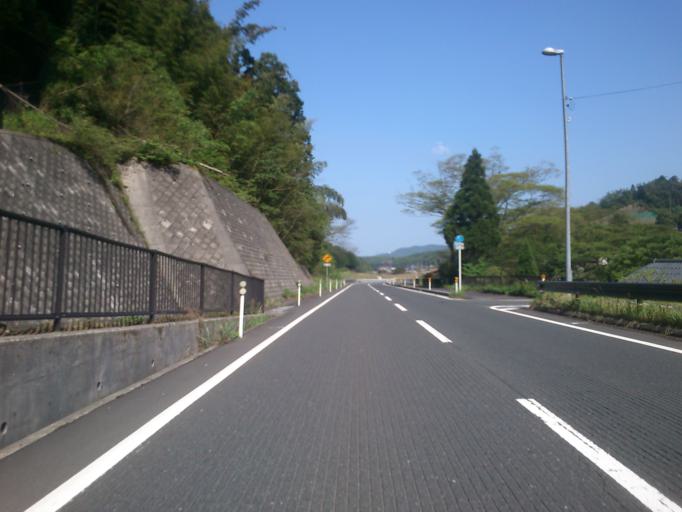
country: JP
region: Kyoto
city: Miyazu
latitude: 35.6478
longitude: 135.1254
